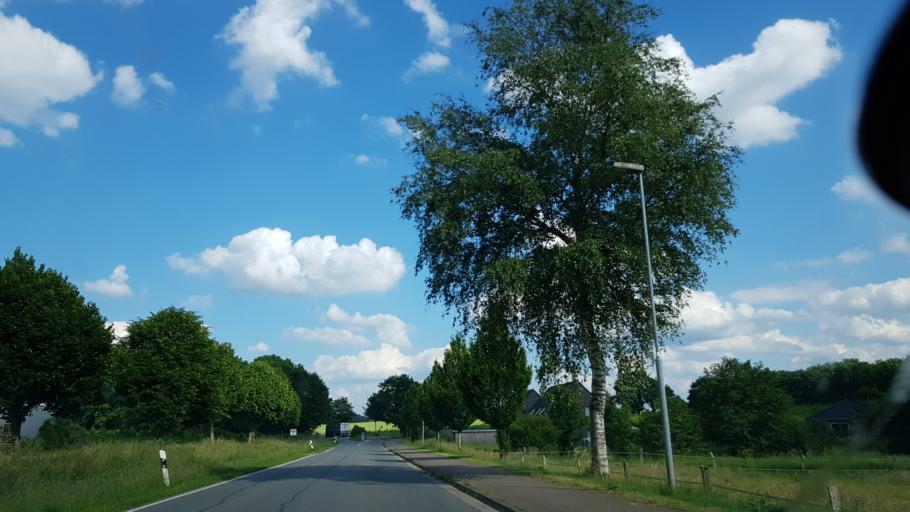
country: DE
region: Lower Saxony
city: Wenzendorf
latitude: 53.3483
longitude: 9.7814
